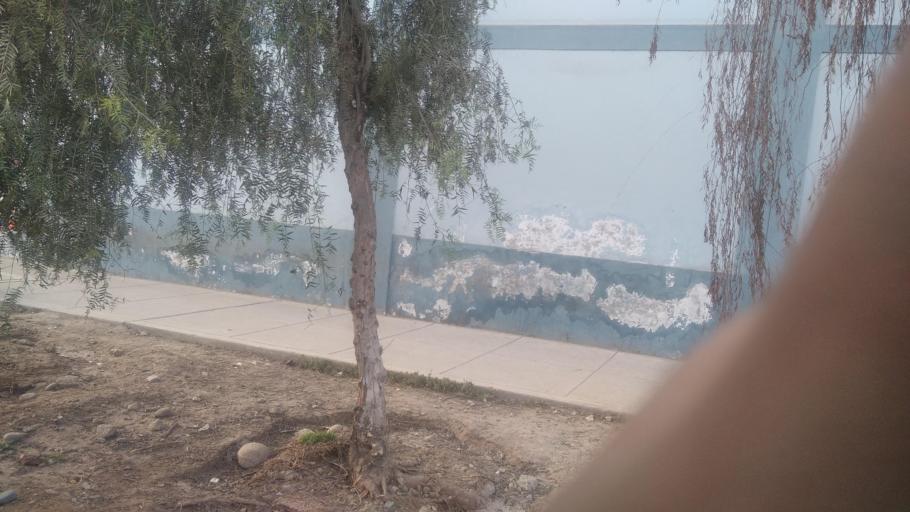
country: PE
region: Lima
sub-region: Lima
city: Vitarte
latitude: -12.0212
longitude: -76.9606
